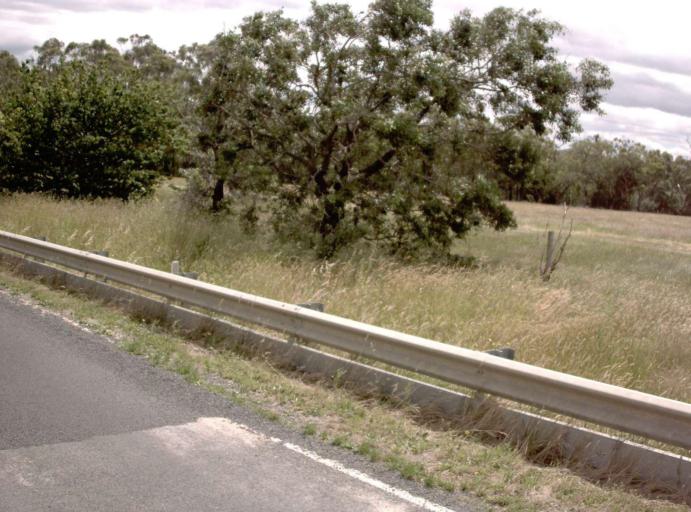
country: AU
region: Victoria
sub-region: Latrobe
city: Moe
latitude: -38.1070
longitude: 146.1582
